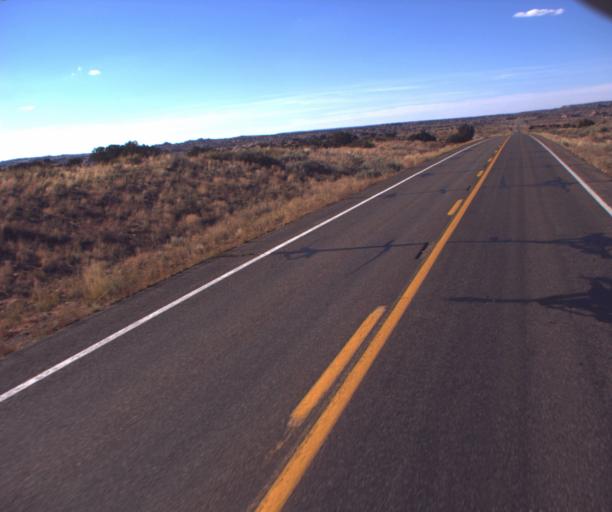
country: US
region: Arizona
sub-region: Coconino County
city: Kaibito
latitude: 36.5975
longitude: -111.1666
